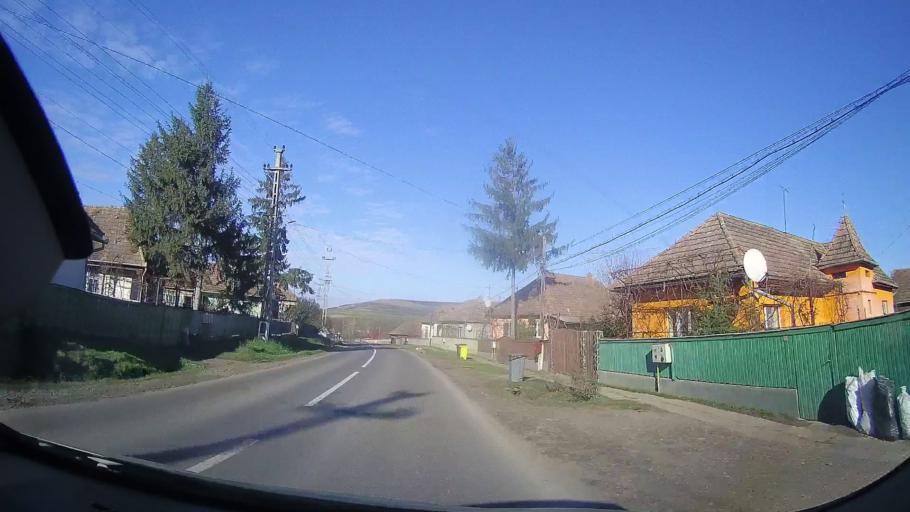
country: RO
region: Mures
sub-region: Comuna Band
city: Band
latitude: 46.5813
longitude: 24.3723
